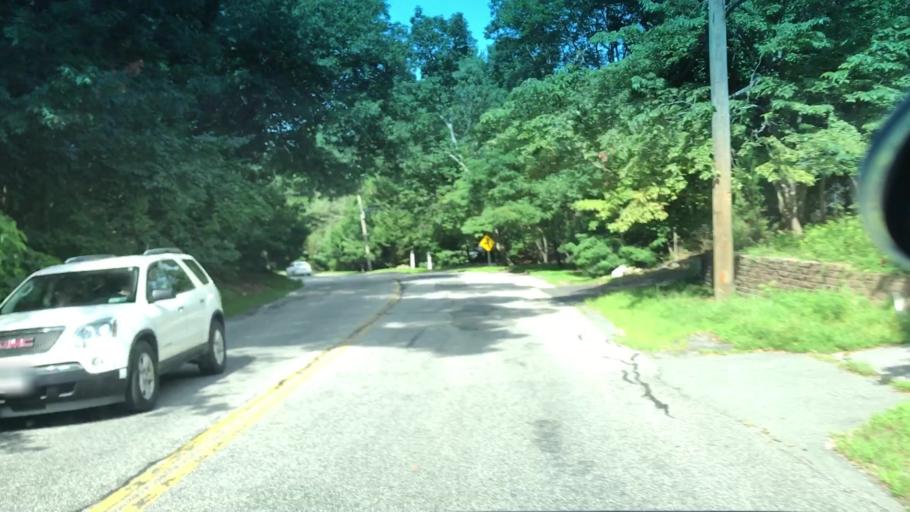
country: US
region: New York
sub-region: Suffolk County
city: Wading River
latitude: 40.9592
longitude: -72.8371
